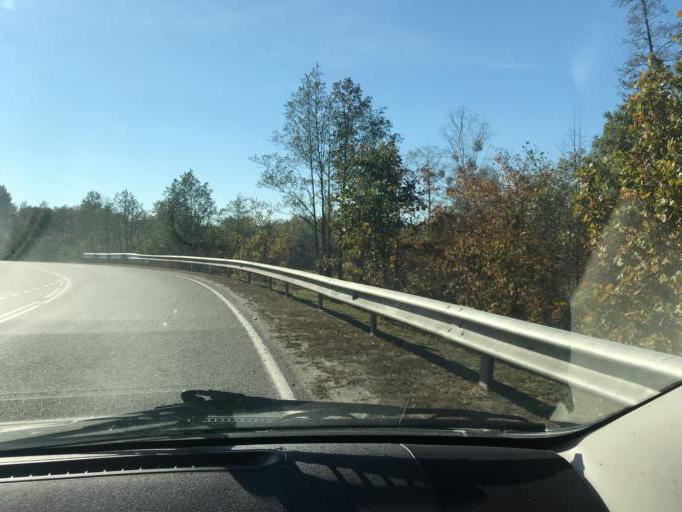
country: BY
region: Brest
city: Mikashevichy
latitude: 52.2459
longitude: 27.4421
